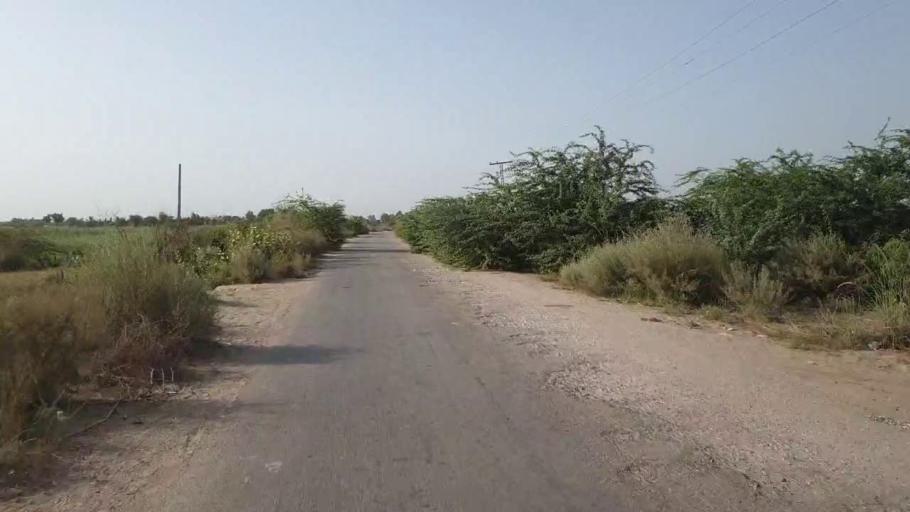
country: PK
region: Sindh
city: Jam Sahib
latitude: 26.4231
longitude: 68.8718
